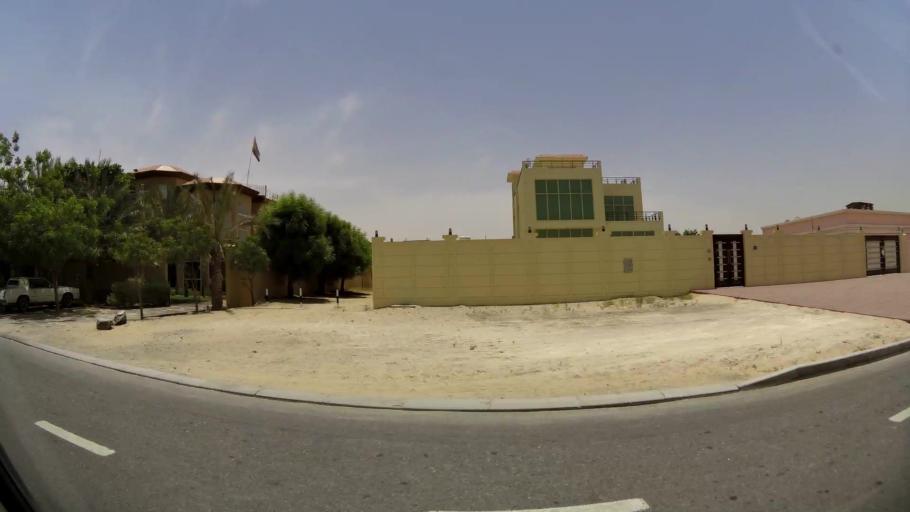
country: AE
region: Ash Shariqah
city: Sharjah
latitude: 25.2516
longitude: 55.4502
